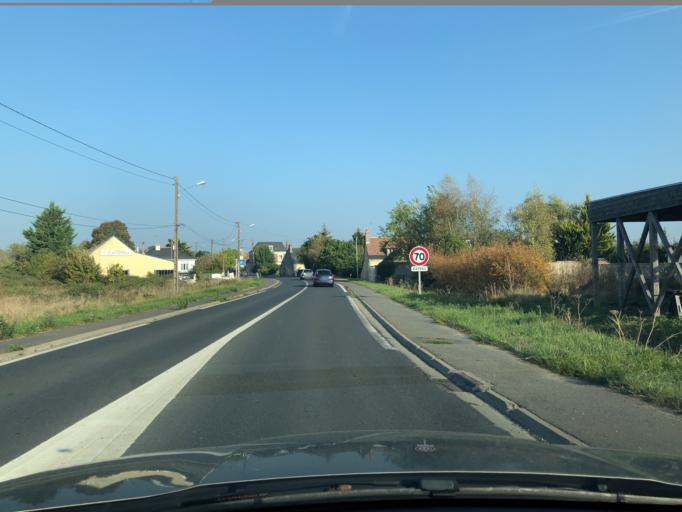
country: FR
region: Centre
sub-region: Departement d'Indre-et-Loire
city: Chanceaux-sur-Choisille
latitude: 47.4437
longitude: 0.6998
